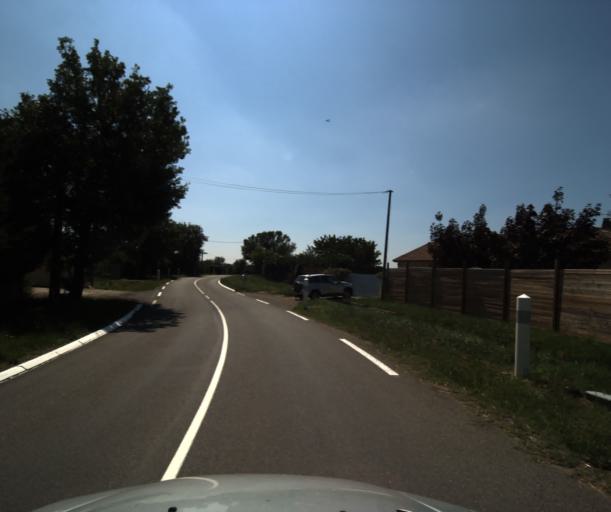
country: FR
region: Midi-Pyrenees
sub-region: Departement de la Haute-Garonne
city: Labastidette
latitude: 43.4373
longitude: 1.2526
